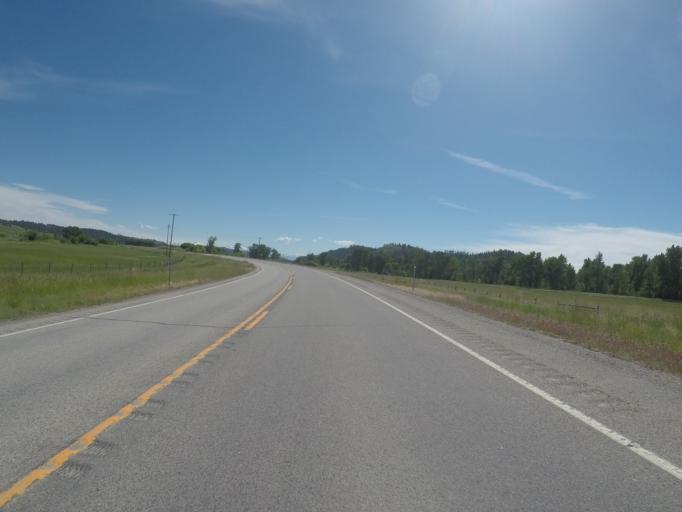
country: US
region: Montana
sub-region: Stillwater County
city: Columbus
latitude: 45.6314
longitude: -109.2776
